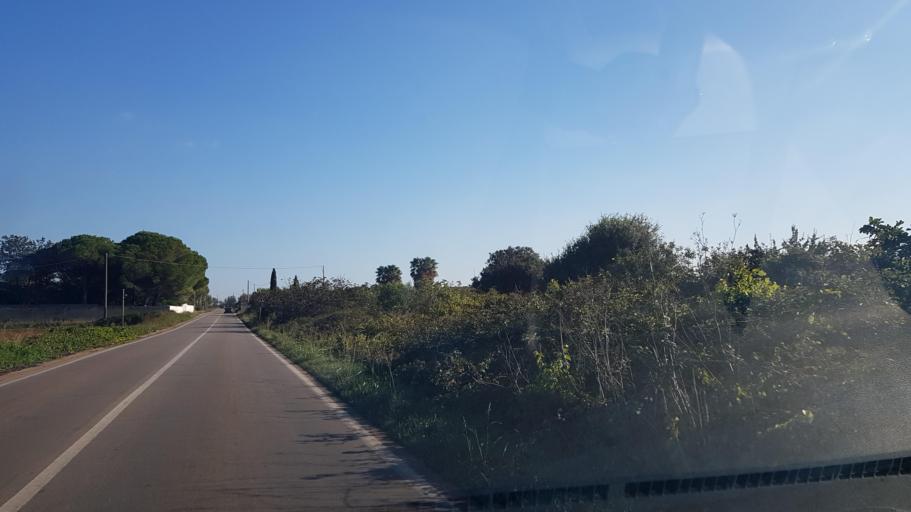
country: IT
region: Apulia
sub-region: Provincia di Lecce
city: Montesano Salentino
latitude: 39.9654
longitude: 18.3323
